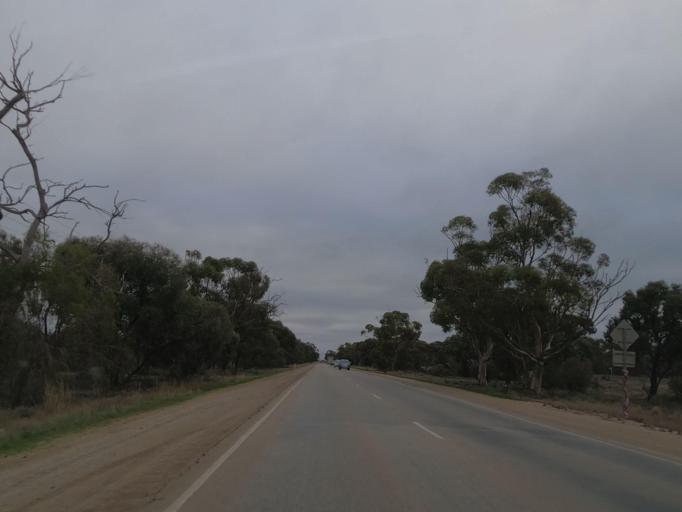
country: AU
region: Victoria
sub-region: Swan Hill
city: Swan Hill
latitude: -35.4043
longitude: 143.5800
